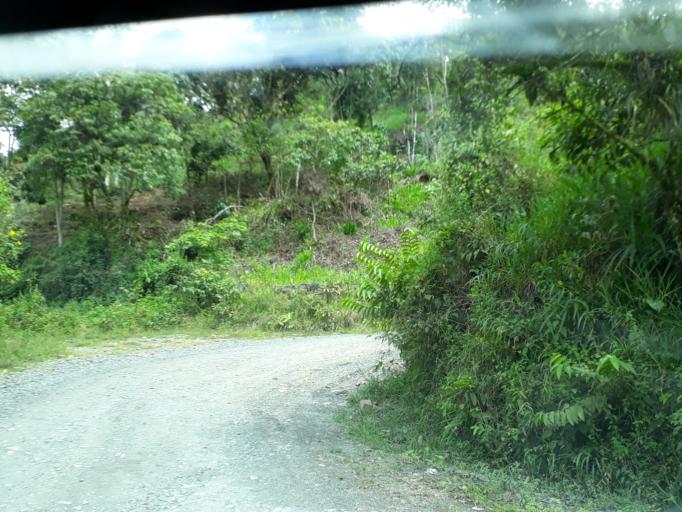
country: CO
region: Cundinamarca
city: Topaipi
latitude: 5.2951
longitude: -74.1931
